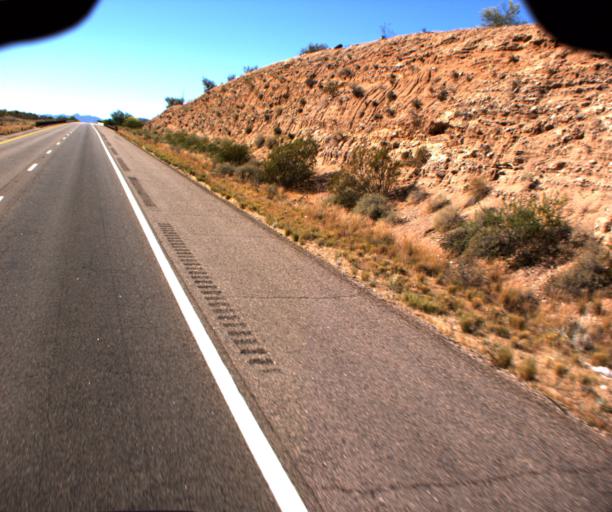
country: US
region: Arizona
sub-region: Yavapai County
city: Bagdad
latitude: 34.6165
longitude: -113.5285
